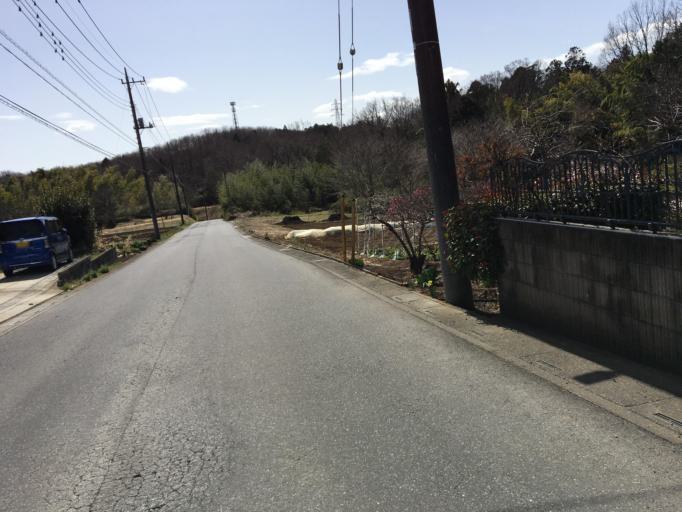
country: JP
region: Saitama
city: Ogawa
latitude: 36.0184
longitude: 139.3277
